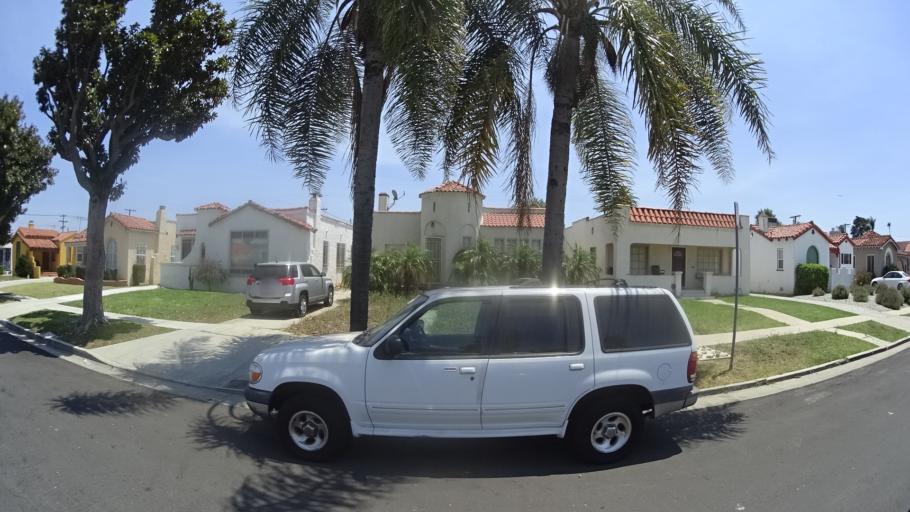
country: US
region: California
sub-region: Los Angeles County
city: Westmont
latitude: 33.9684
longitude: -118.3035
